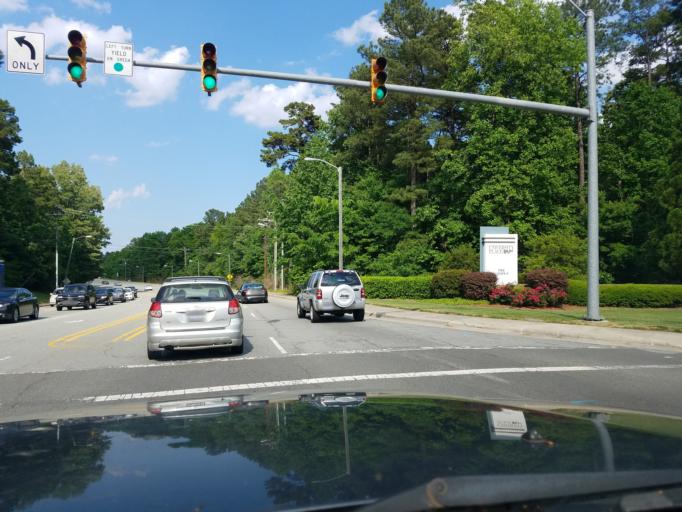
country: US
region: North Carolina
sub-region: Durham County
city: Durham
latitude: 35.9596
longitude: -78.9643
